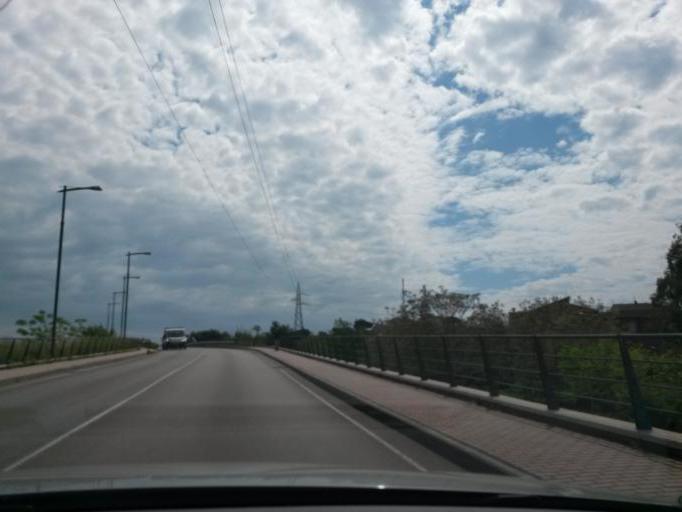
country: IT
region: Tuscany
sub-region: Provincia di Livorno
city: Piombino
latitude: 42.9261
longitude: 10.5353
